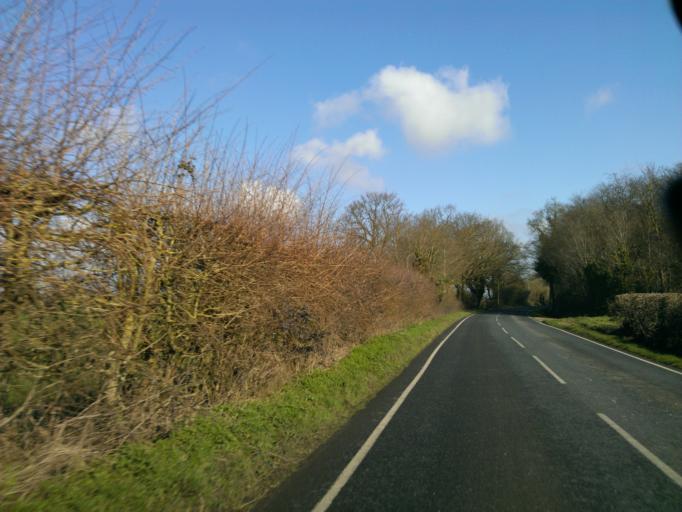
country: GB
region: England
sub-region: Essex
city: Alresford
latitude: 51.8705
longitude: 0.9909
